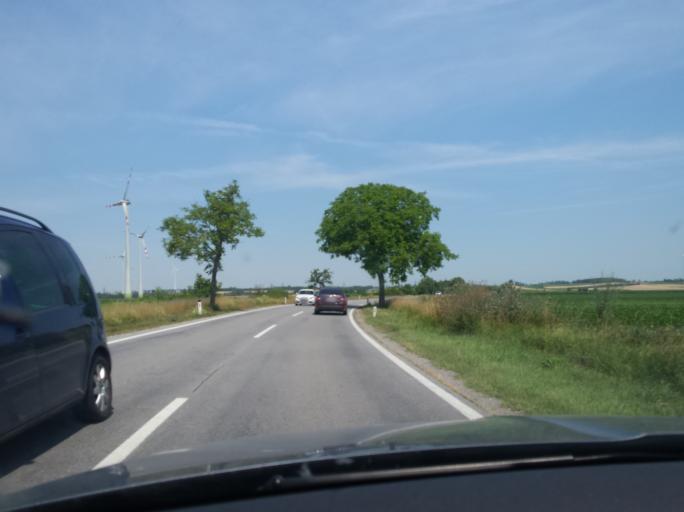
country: AT
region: Lower Austria
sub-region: Politischer Bezirk Bruck an der Leitha
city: Rohrau
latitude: 48.0747
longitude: 16.8607
